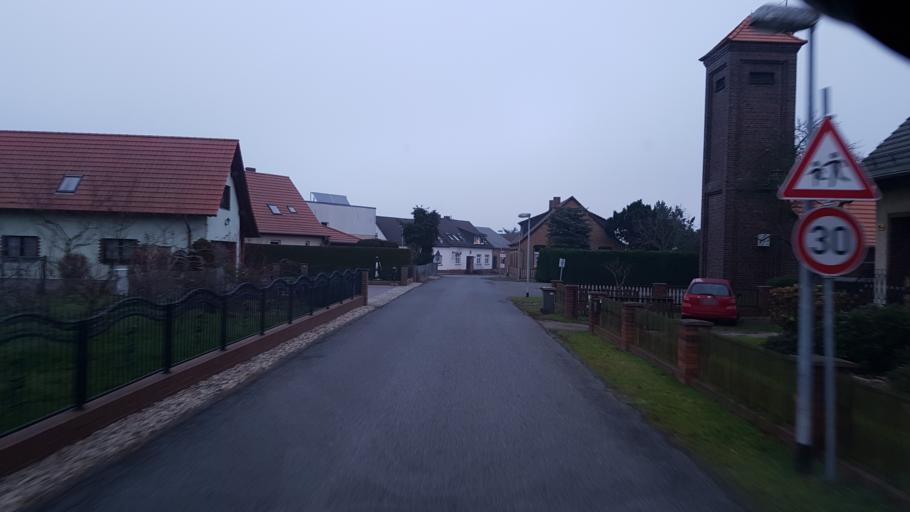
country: DE
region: Brandenburg
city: Altdobern
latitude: 51.6924
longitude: 14.0047
